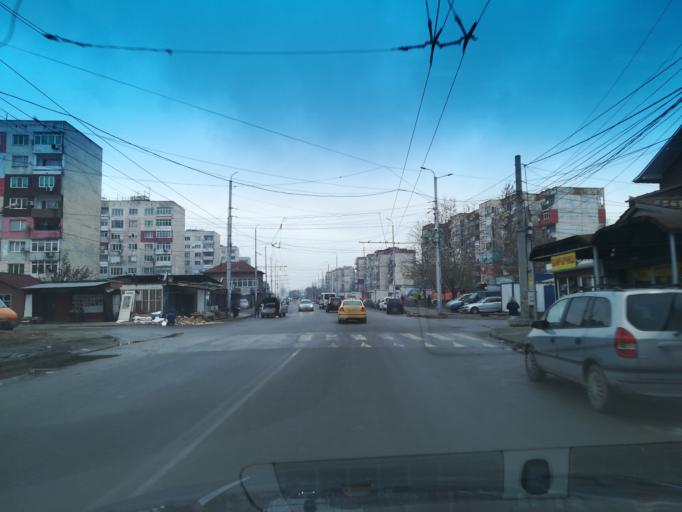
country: BG
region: Plovdiv
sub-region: Obshtina Plovdiv
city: Plovdiv
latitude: 42.1595
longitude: 24.7865
